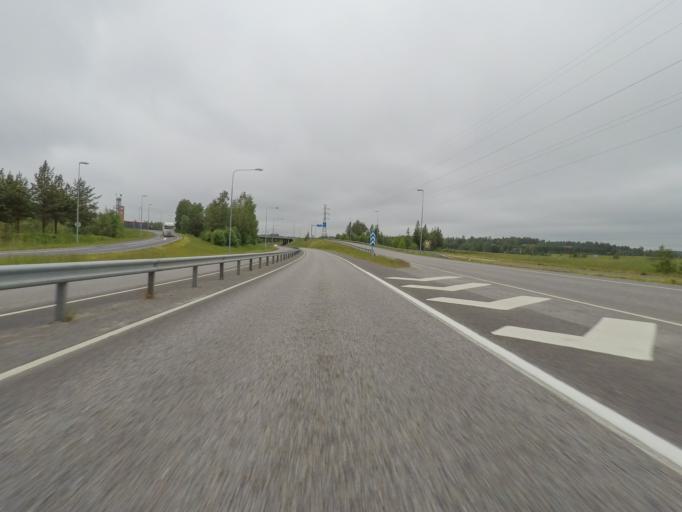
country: FI
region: Varsinais-Suomi
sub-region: Turku
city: Naantali
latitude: 60.4728
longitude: 22.0713
